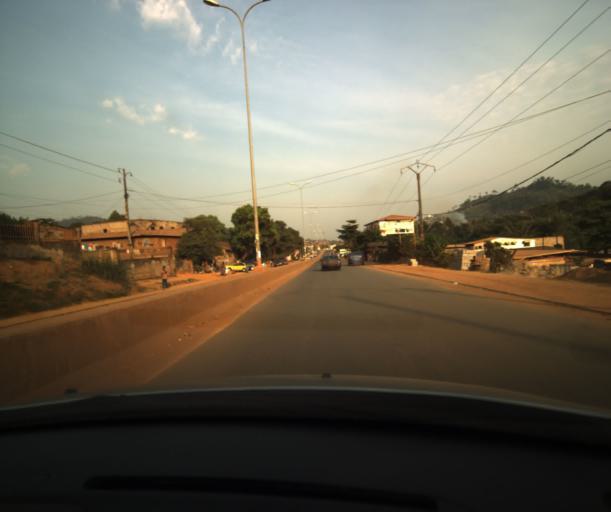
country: CM
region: Centre
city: Yaounde
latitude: 3.8728
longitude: 11.4578
